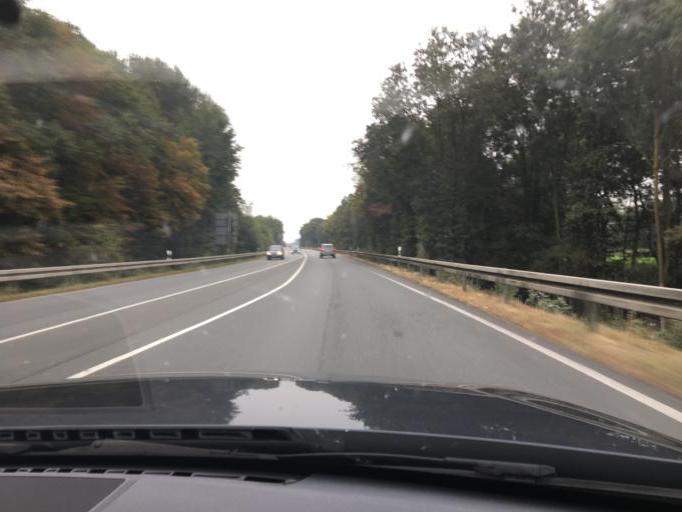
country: DE
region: North Rhine-Westphalia
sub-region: Regierungsbezirk Munster
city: Greven
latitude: 52.0816
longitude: 7.6475
